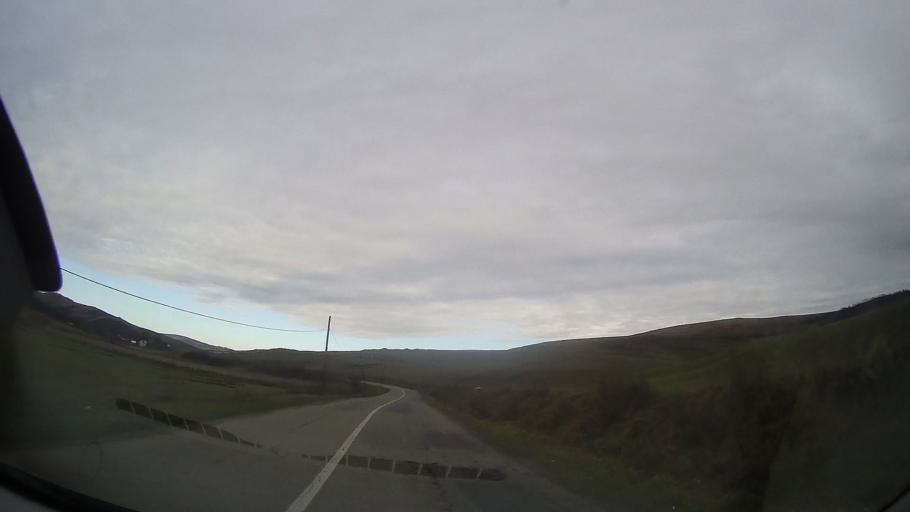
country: RO
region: Cluj
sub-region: Comuna Camarasu
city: Camarasu
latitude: 46.8098
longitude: 24.1436
